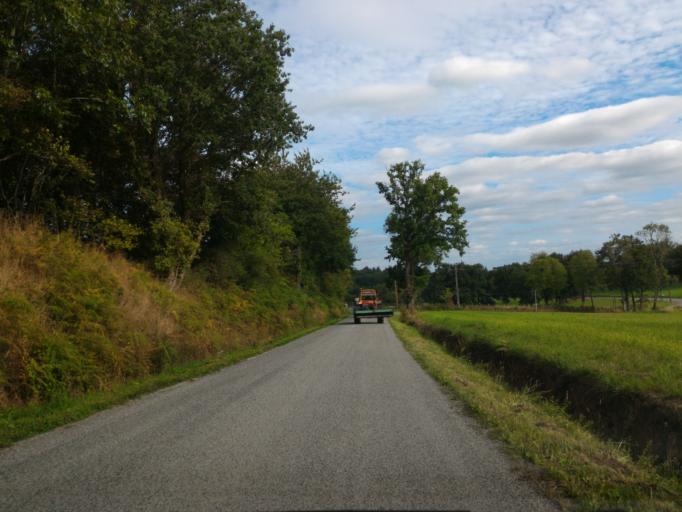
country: FR
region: Poitou-Charentes
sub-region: Departement de la Charente
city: Brigueuil
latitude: 45.9113
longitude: 0.8578
